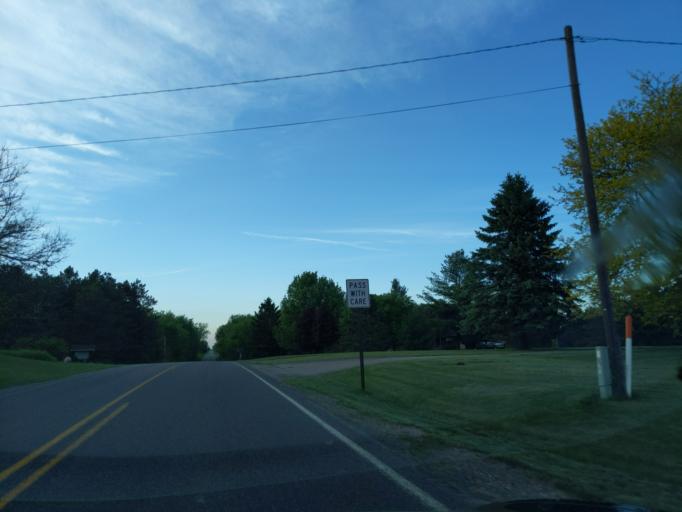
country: US
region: Michigan
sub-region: Ingham County
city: Williamston
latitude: 42.5675
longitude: -84.2983
